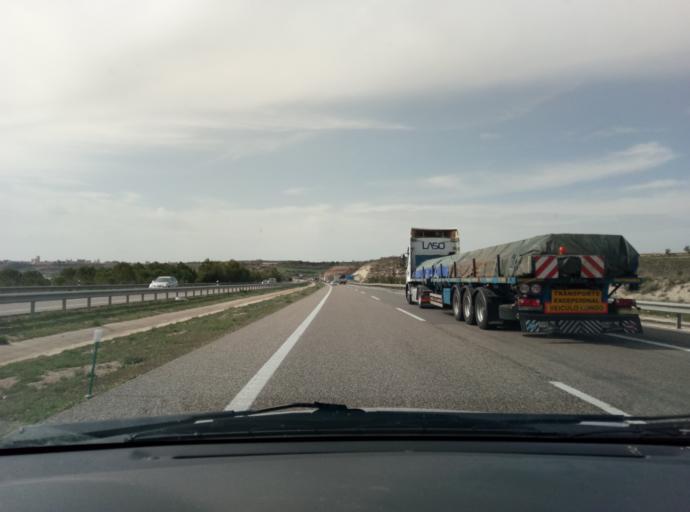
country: ES
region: Catalonia
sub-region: Provincia de Lleida
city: Cervera
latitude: 41.6595
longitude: 1.3094
